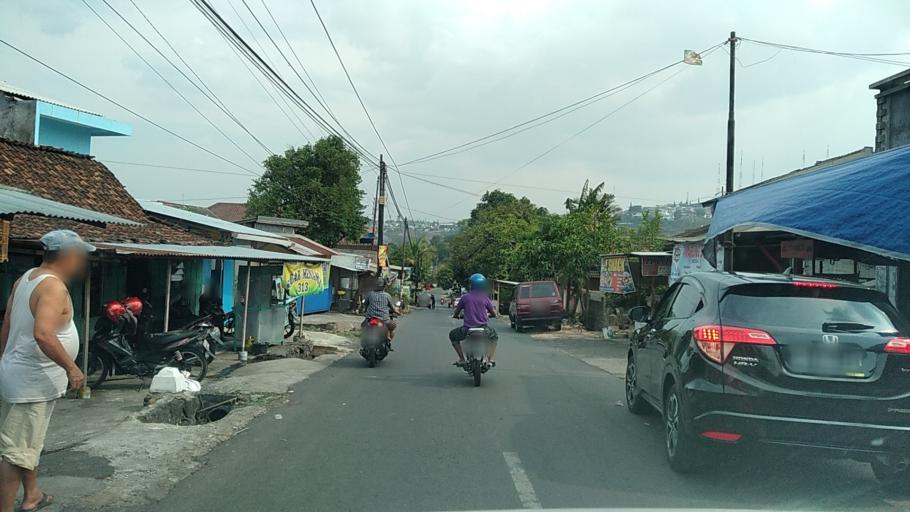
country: ID
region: Central Java
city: Semarang
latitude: -7.0282
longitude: 110.4285
